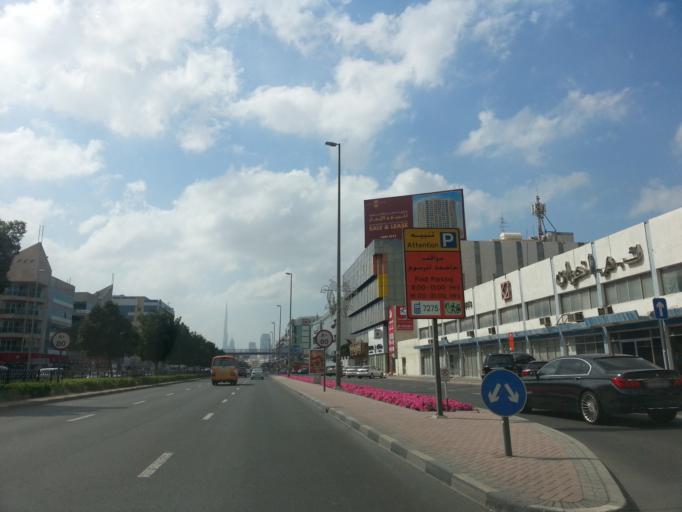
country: AE
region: Ash Shariqah
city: Sharjah
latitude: 25.2442
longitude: 55.3108
